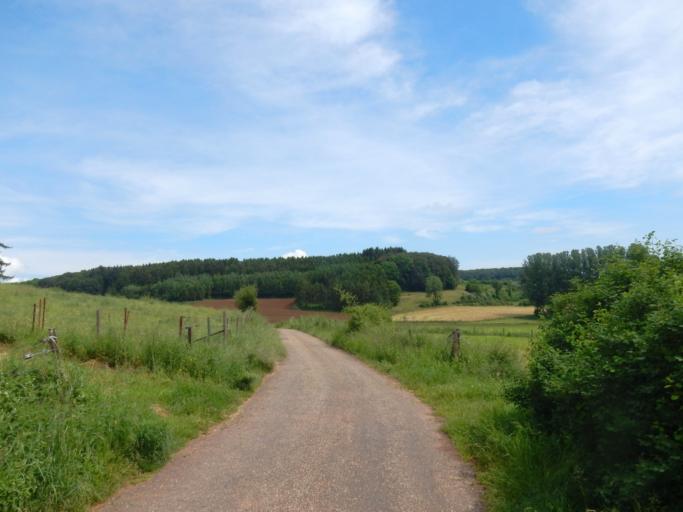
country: LU
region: Diekirch
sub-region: Canton de Redange
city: Vichten
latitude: 49.8037
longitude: 6.0053
